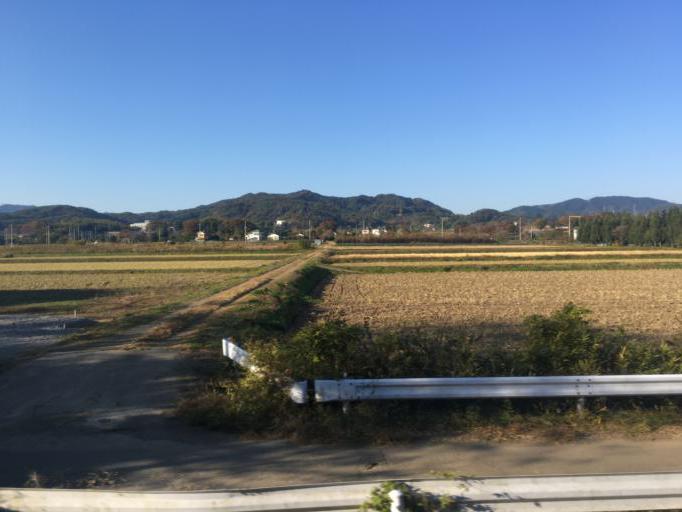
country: JP
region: Saitama
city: Yorii
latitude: 36.1472
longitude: 139.2047
